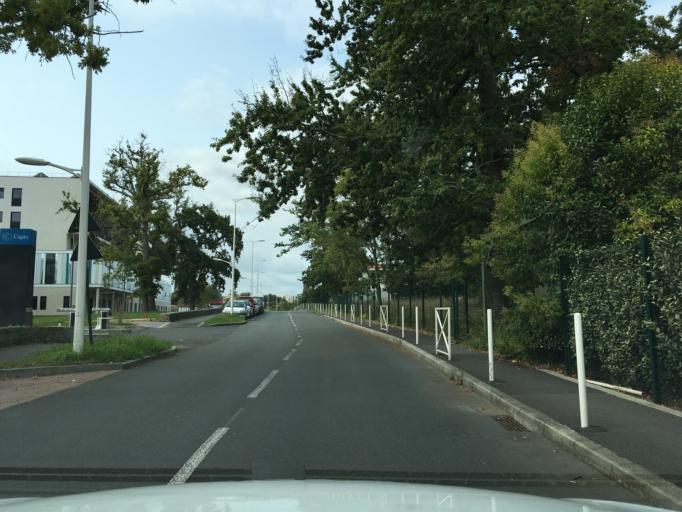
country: FR
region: Aquitaine
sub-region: Departement des Pyrenees-Atlantiques
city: Bayonne
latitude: 43.4804
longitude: -1.4524
